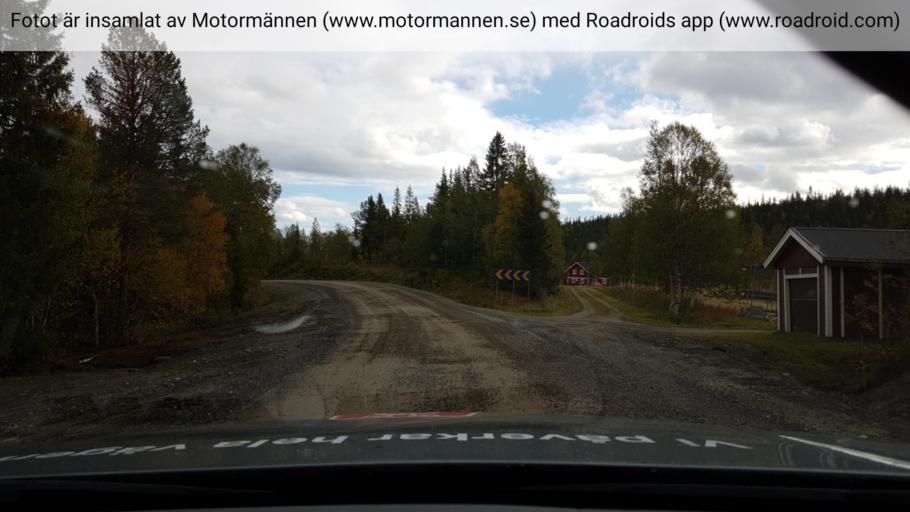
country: NO
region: Nord-Trondelag
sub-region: Snasa
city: Snaase
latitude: 63.7127
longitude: 12.4572
